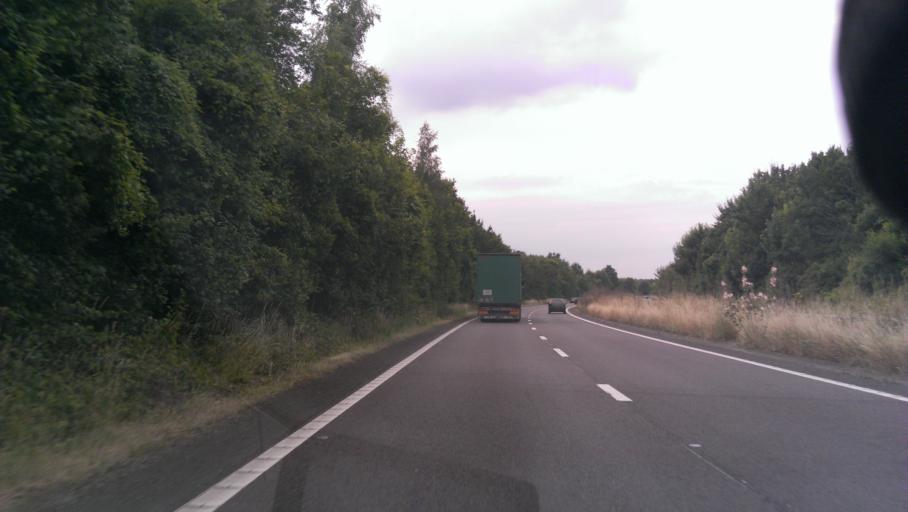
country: GB
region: England
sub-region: Kent
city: Canterbury
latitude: 51.2558
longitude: 1.0817
